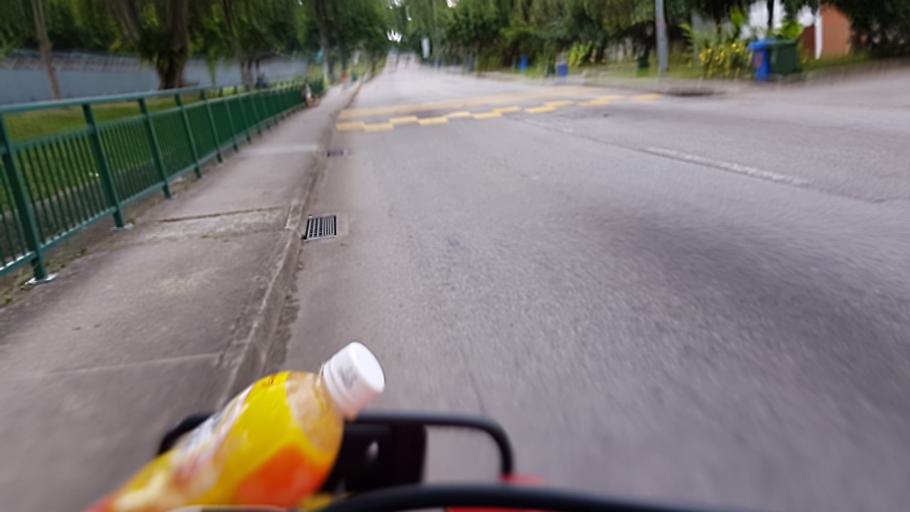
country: MY
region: Johor
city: Kampung Pasir Gudang Baru
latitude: 1.3656
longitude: 103.9754
